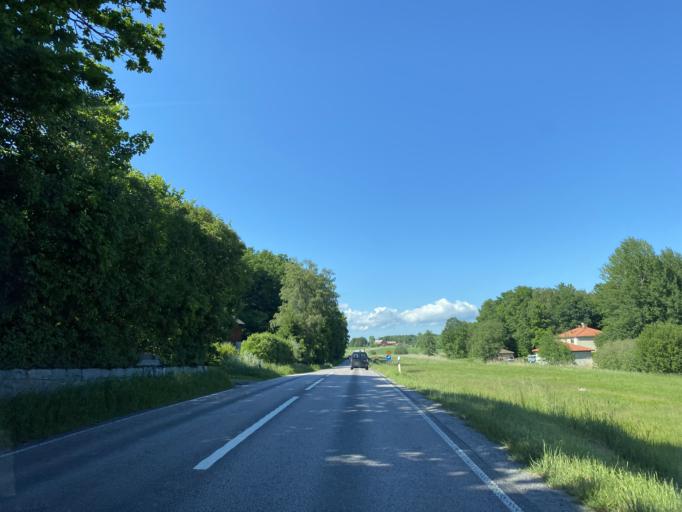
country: SE
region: Stockholm
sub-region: Norrtalje Kommun
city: Norrtalje
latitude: 59.8073
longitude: 18.6499
